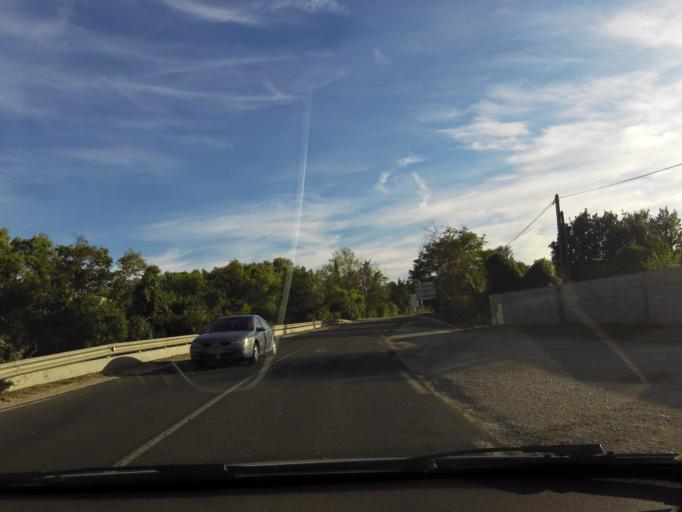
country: FR
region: Languedoc-Roussillon
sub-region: Departement de l'Herault
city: Prades-le-Lez
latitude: 43.7043
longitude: 3.8679
